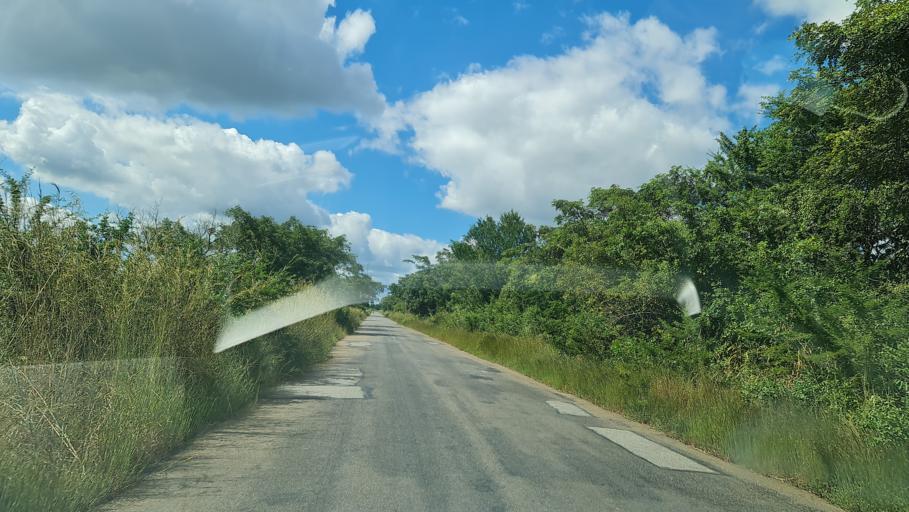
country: MZ
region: Zambezia
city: Quelimane
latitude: -17.5088
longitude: 36.2359
